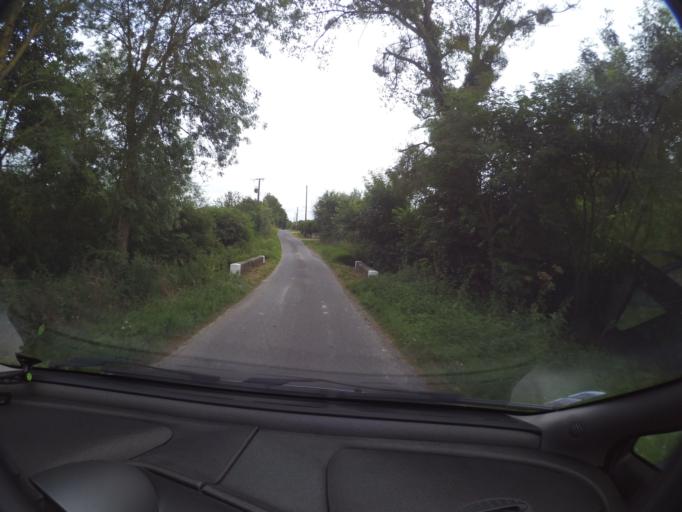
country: FR
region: Pays de la Loire
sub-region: Departement de la Loire-Atlantique
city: Saint-Hilaire-de-Clisson
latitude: 47.0351
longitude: -1.3046
